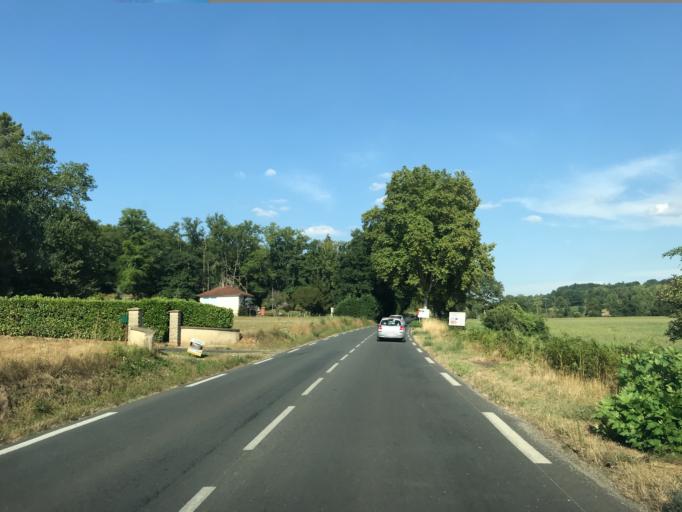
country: FR
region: Midi-Pyrenees
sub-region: Departement du Lot
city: Le Vigan
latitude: 44.7408
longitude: 1.4143
